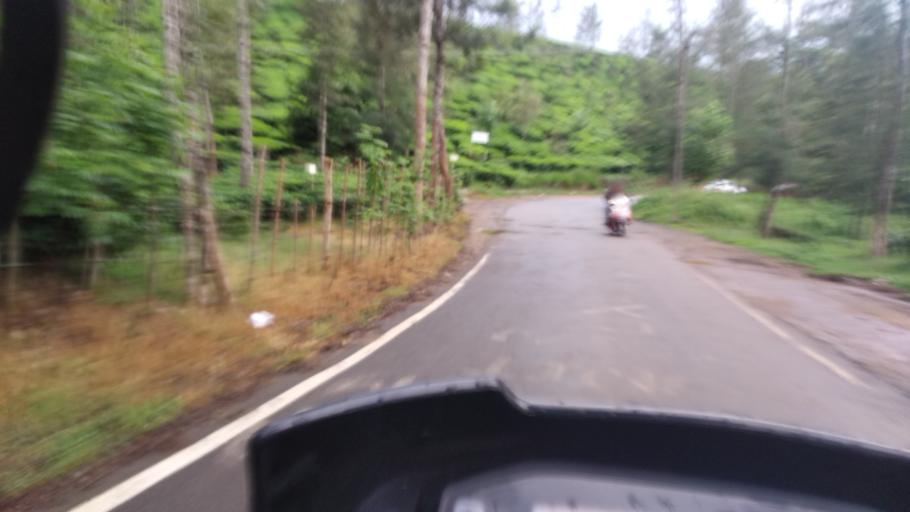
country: IN
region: Tamil Nadu
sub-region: Theni
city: Gudalur
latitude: 9.5677
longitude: 77.0819
